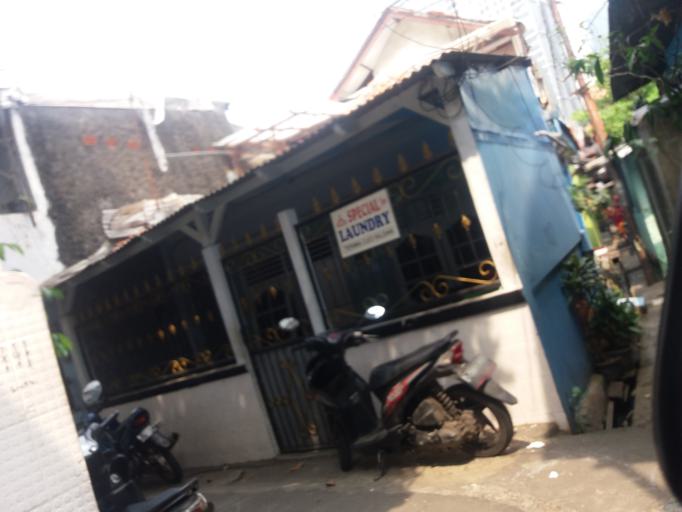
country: ID
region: Jakarta Raya
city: Jakarta
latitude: -6.1894
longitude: 106.8204
